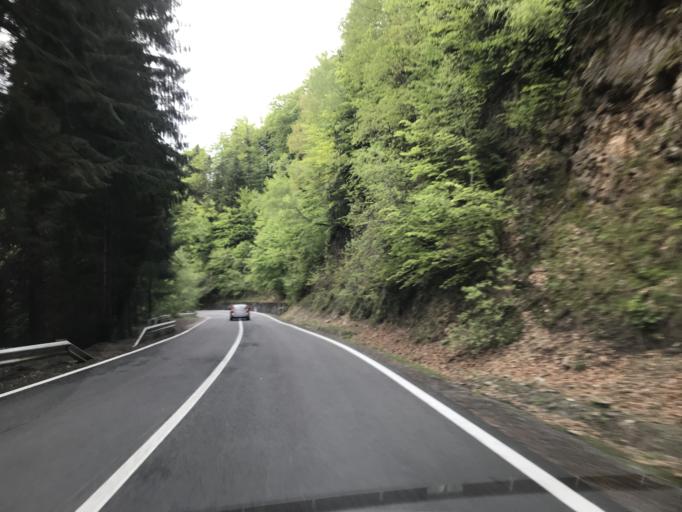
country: RO
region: Sibiu
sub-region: Comuna Cartisoara
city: Cartisoara
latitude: 45.6669
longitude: 24.5941
